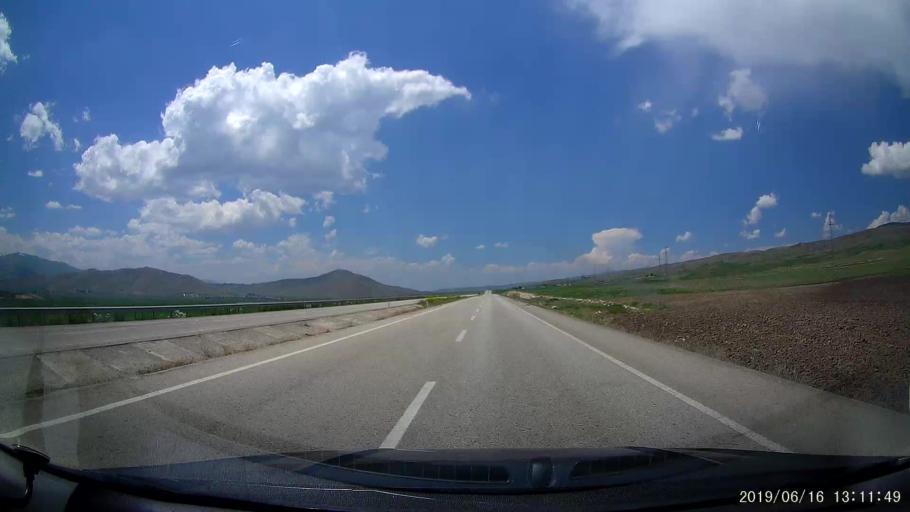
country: TR
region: Agri
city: Diyadin
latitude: 39.5941
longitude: 43.5967
